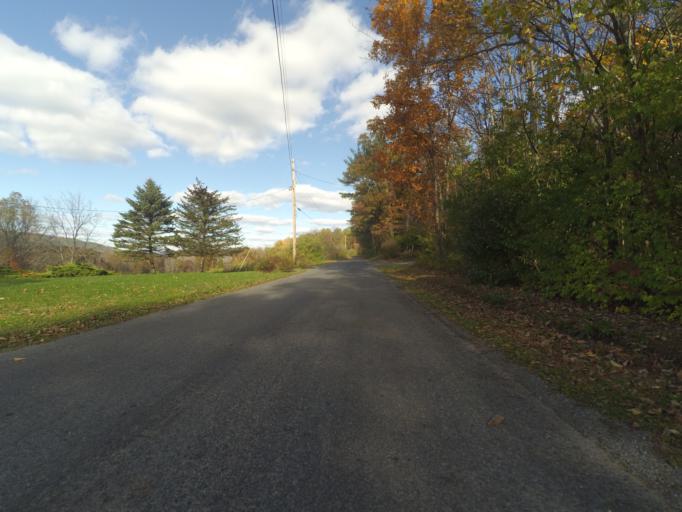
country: US
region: Pennsylvania
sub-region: Centre County
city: Bellefonte
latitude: 40.8817
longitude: -77.7996
